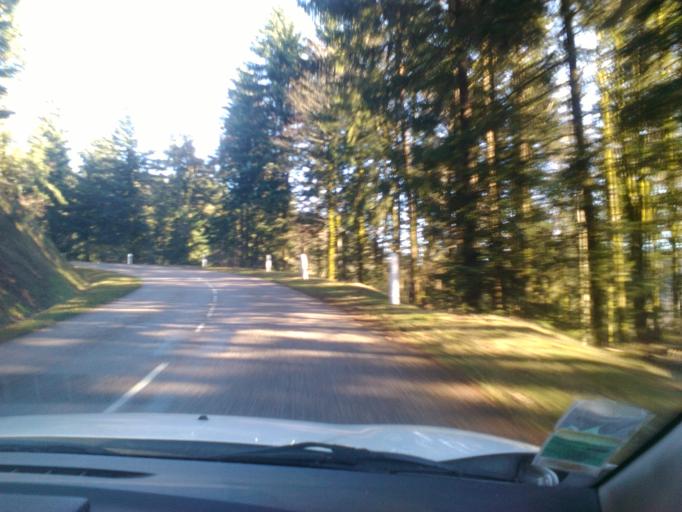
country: FR
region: Lorraine
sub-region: Departement des Vosges
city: Remiremont
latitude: 47.9738
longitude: 6.5392
